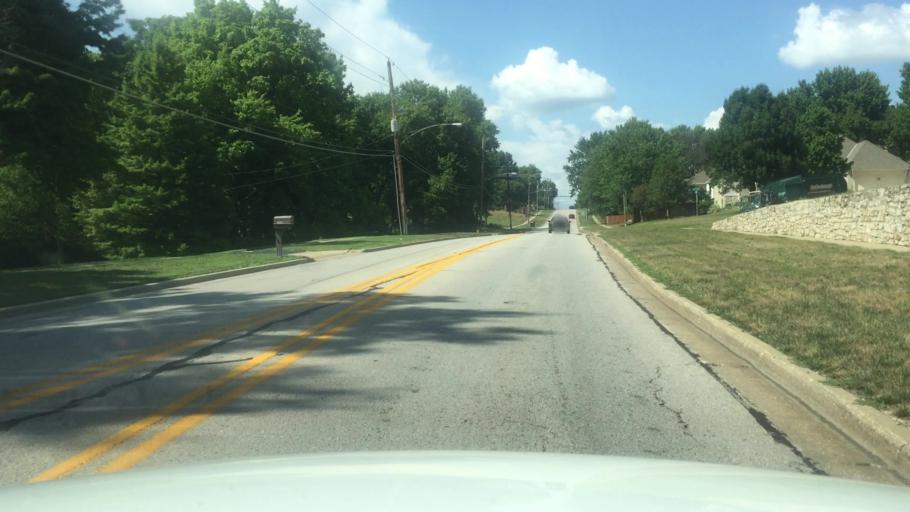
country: US
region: Kansas
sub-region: Johnson County
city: Shawnee
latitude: 39.0008
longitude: -94.7424
